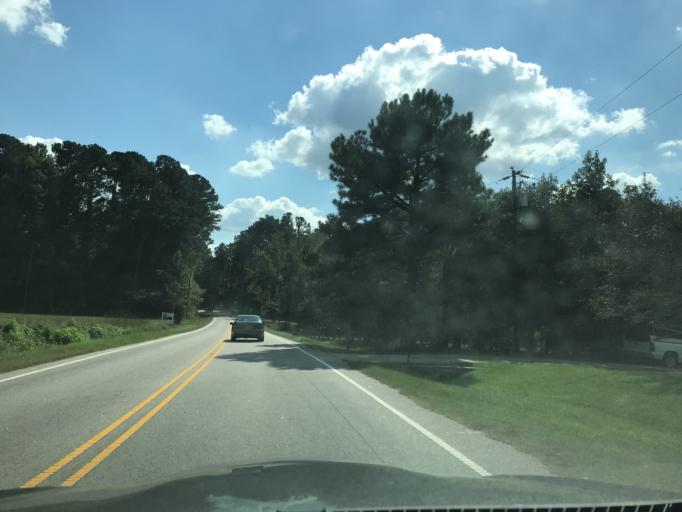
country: US
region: North Carolina
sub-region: Wake County
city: Rolesville
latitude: 35.8907
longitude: -78.5268
